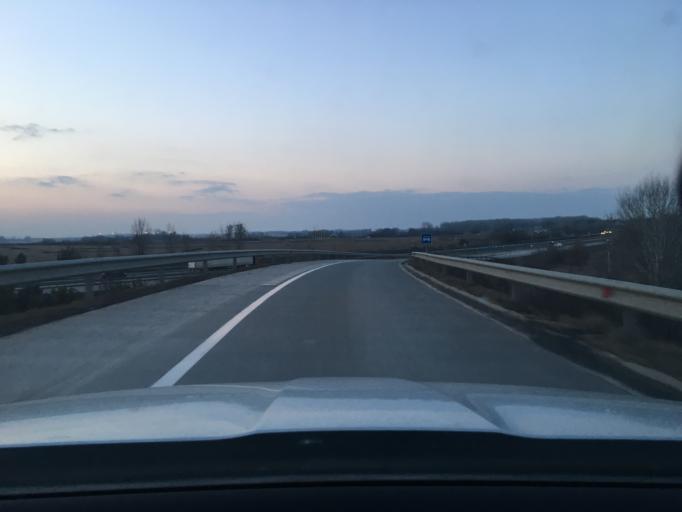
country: HU
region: Pest
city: Vecses
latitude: 47.4058
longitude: 19.3175
